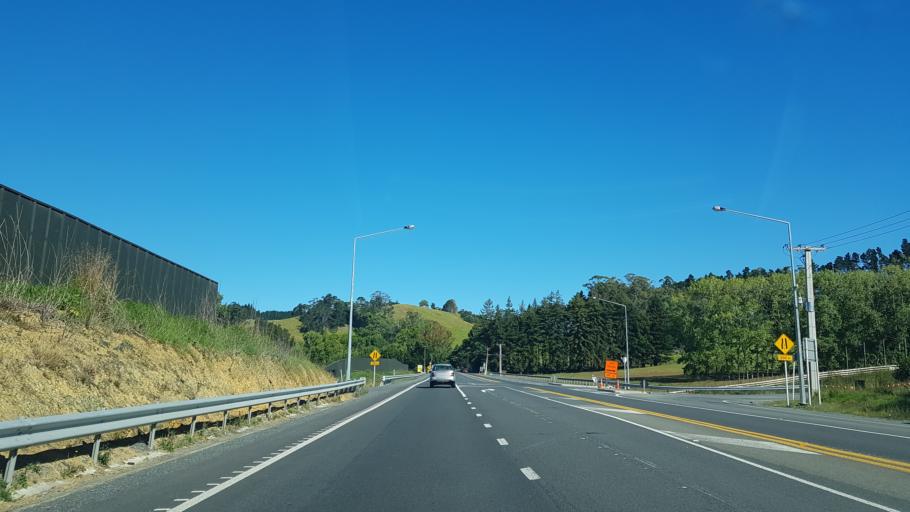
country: NZ
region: Auckland
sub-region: Auckland
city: Warkworth
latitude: -36.4391
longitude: 174.6487
